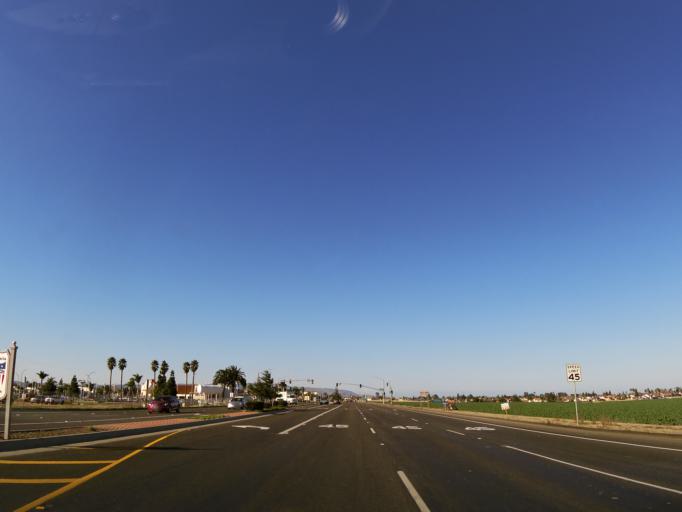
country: US
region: California
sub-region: Santa Barbara County
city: Santa Maria
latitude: 34.9237
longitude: -120.4201
